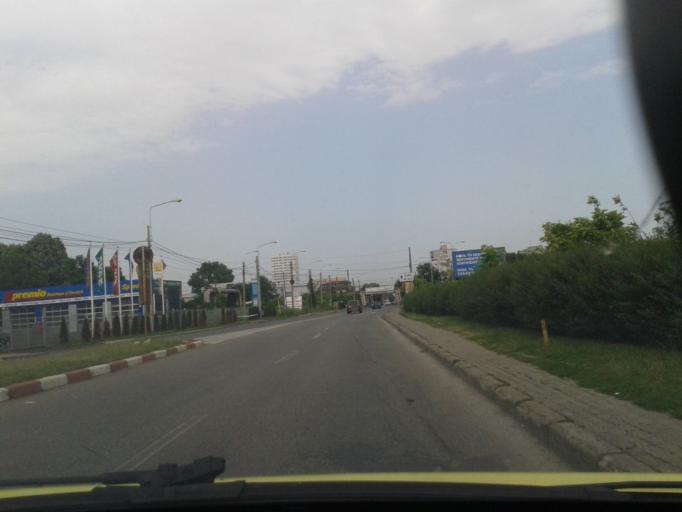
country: RO
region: Prahova
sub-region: Comuna Targsoru Vechi
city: Strejnicu
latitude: 44.9392
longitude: 25.9779
